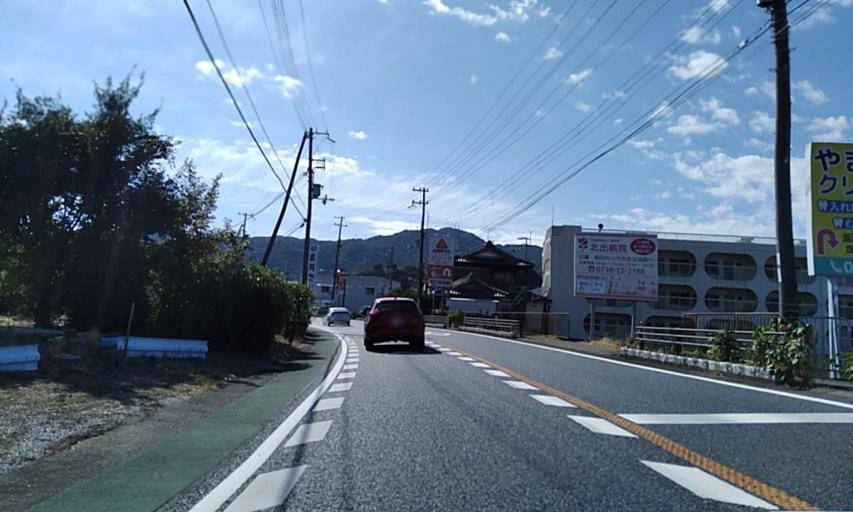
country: JP
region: Wakayama
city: Kainan
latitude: 34.0222
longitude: 135.1792
